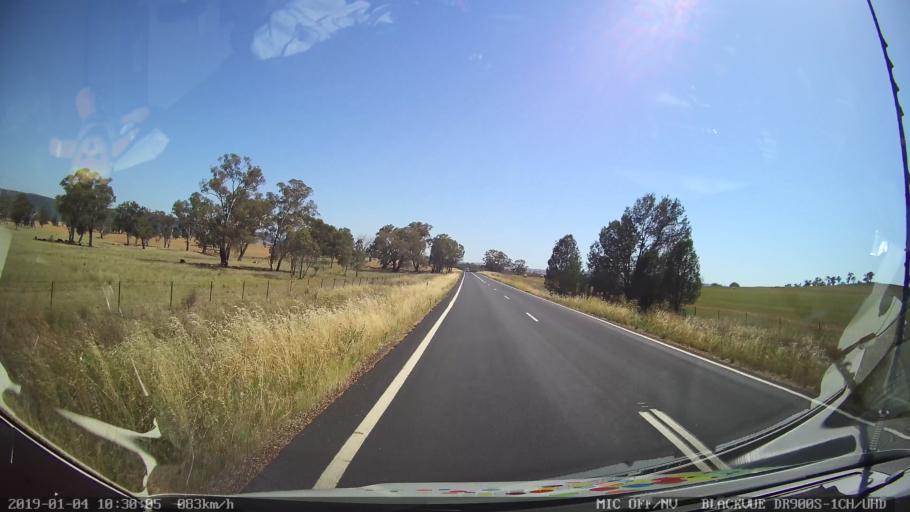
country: AU
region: New South Wales
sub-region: Cabonne
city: Canowindra
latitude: -33.3498
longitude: 148.6258
